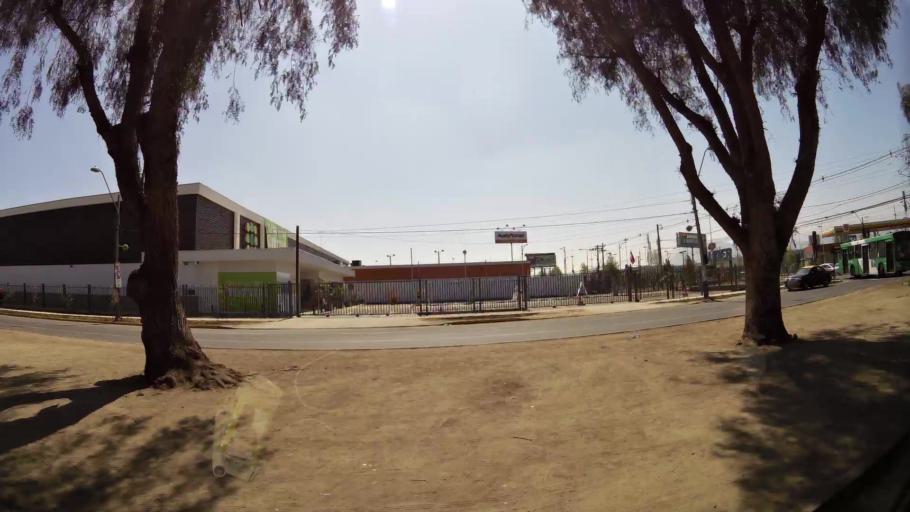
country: CL
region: Santiago Metropolitan
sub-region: Provincia de Santiago
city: Lo Prado
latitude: -33.3578
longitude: -70.7295
